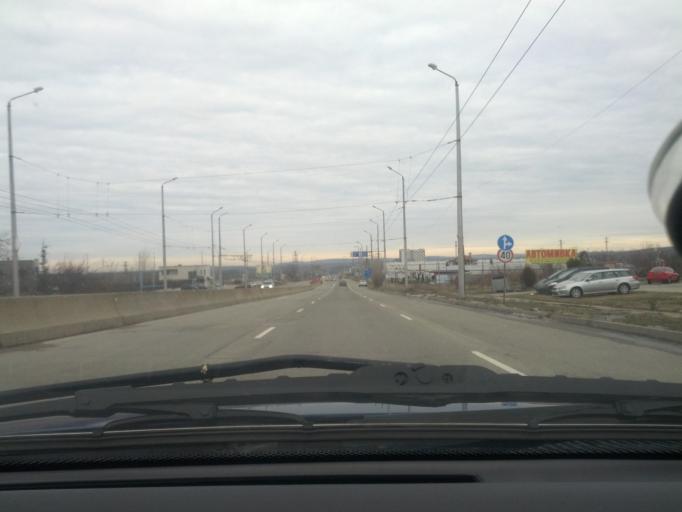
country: BG
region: Vratsa
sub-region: Obshtina Vratsa
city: Vratsa
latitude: 43.2235
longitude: 23.5598
